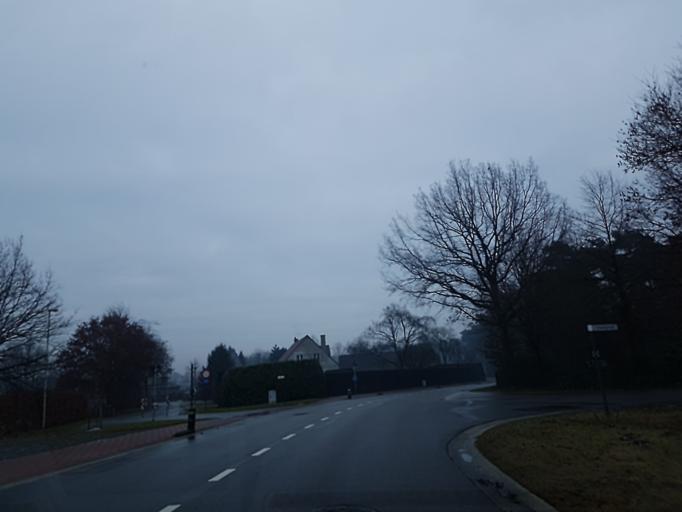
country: BE
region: Flanders
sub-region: Provincie Antwerpen
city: Nijlen
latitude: 51.1632
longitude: 4.6458
